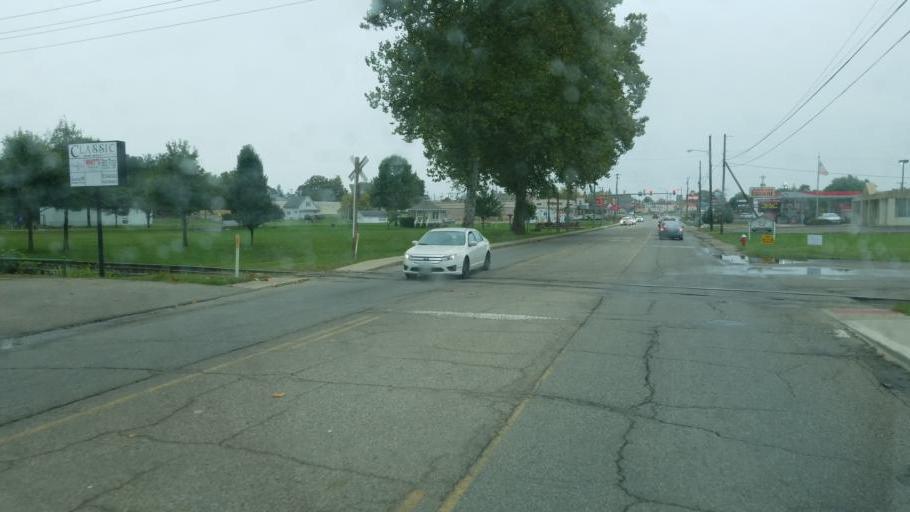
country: US
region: Ohio
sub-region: Jackson County
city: Jackson
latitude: 39.0459
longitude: -82.6307
